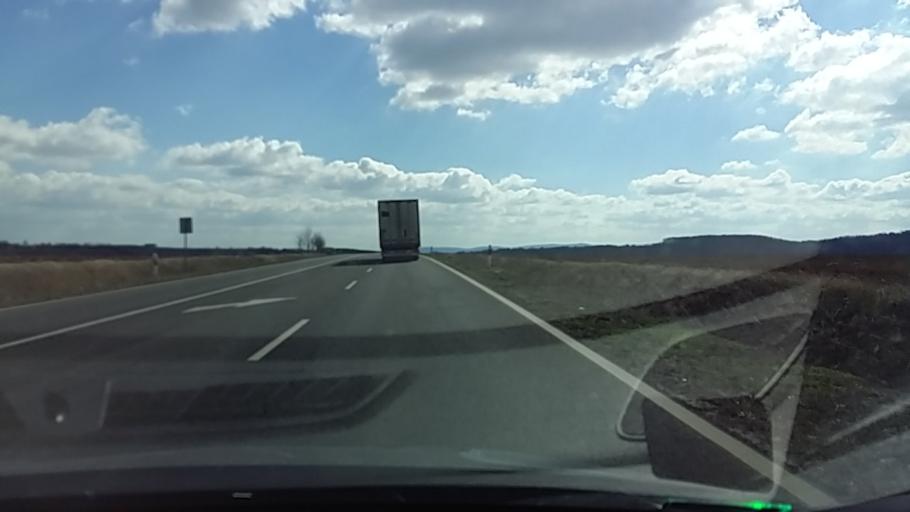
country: HU
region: Baranya
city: Kozarmisleny
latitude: 46.0353
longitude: 18.2729
